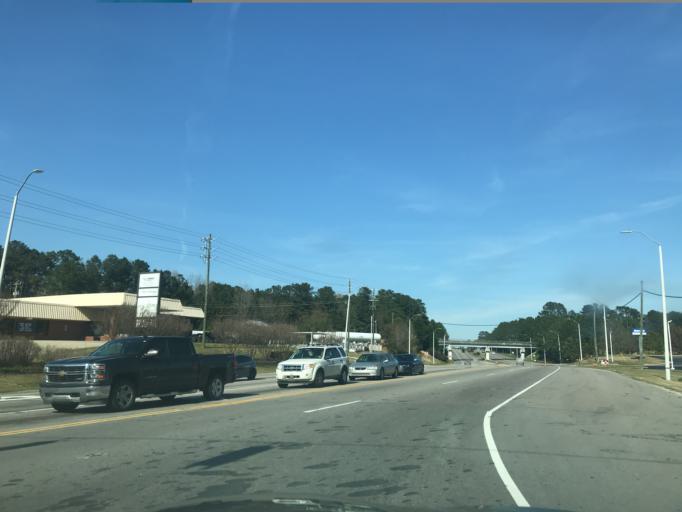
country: US
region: North Carolina
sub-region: Wake County
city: Fuquay-Varina
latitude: 35.5967
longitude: -78.7590
